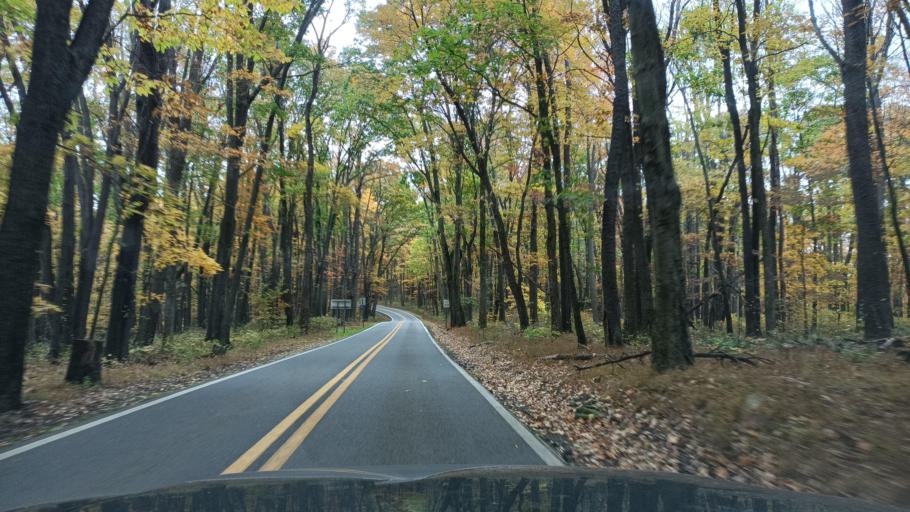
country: US
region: West Virginia
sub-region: Monongalia County
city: Cheat Lake
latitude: 39.6466
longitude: -79.7871
